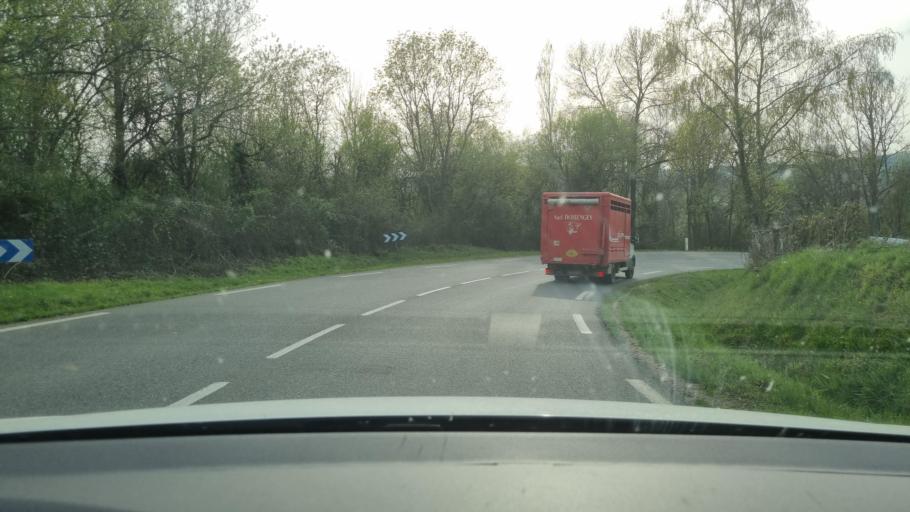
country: FR
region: Aquitaine
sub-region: Departement des Pyrenees-Atlantiques
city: Soumoulou
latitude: 43.3729
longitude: -0.1059
